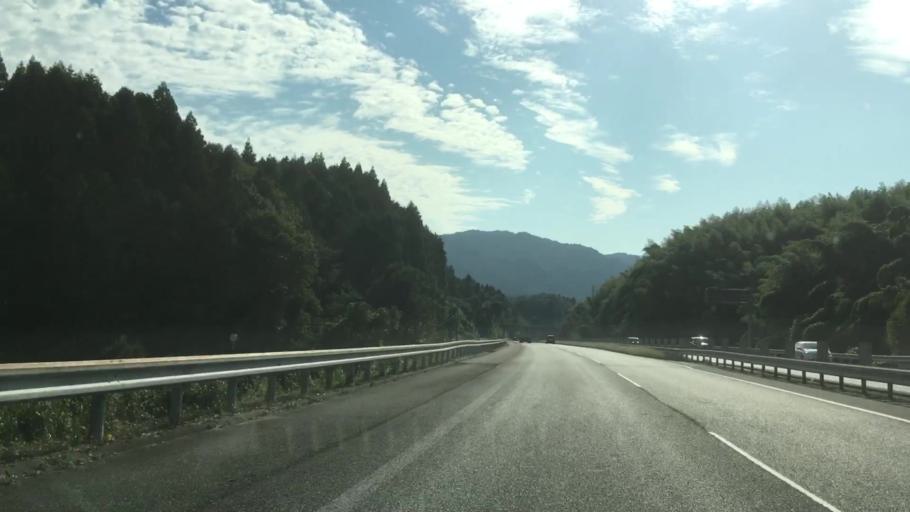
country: JP
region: Yamaguchi
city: Hikari
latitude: 34.0328
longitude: 131.9680
